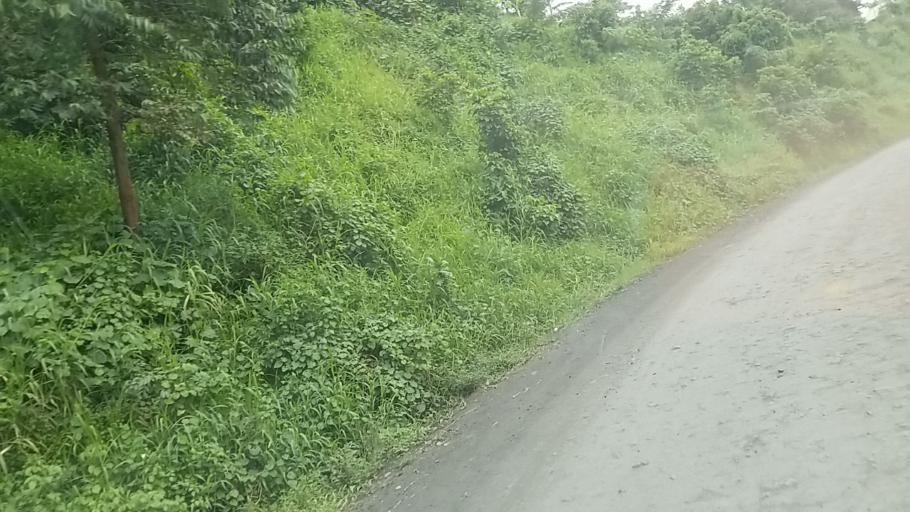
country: CD
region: Nord Kivu
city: Sake
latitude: -1.7581
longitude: 28.9867
